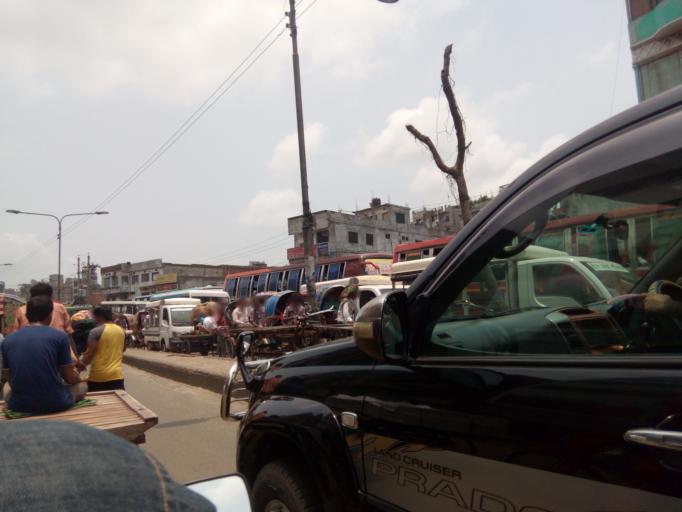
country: BD
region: Dhaka
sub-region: Dhaka
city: Dhaka
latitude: 23.7146
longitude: 90.4082
